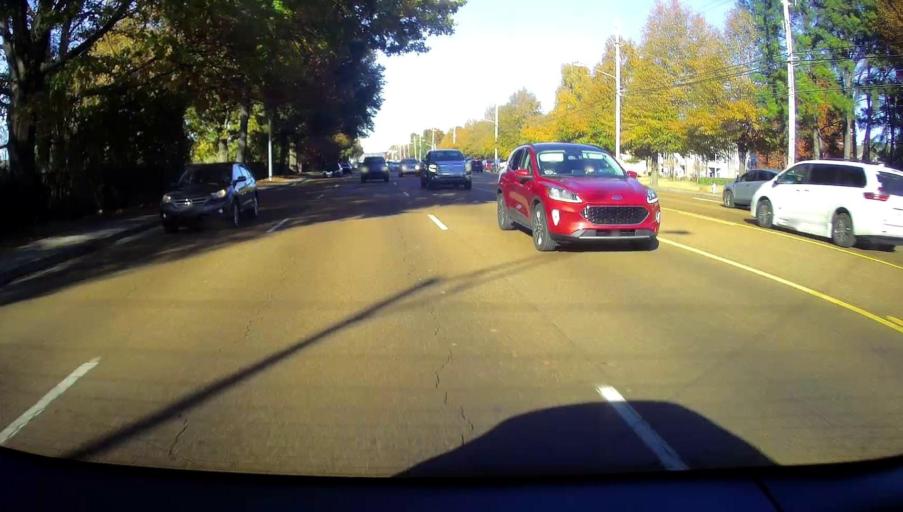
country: US
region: Tennessee
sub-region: Shelby County
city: Germantown
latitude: 35.1083
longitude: -89.8033
